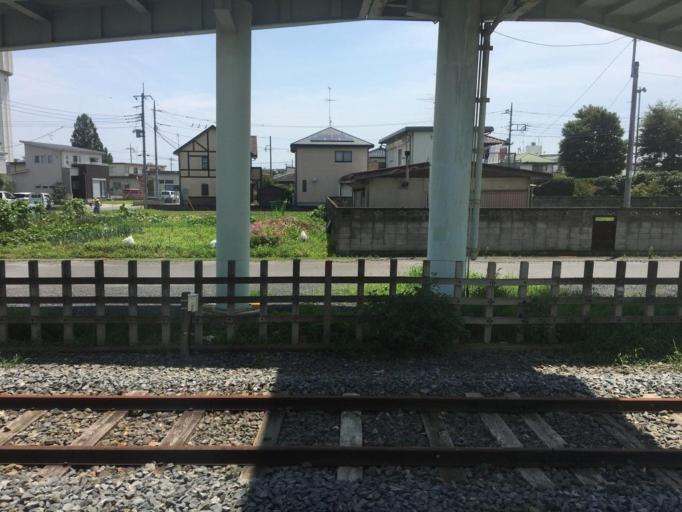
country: JP
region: Saitama
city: Menuma
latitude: 36.2604
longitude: 139.4095
